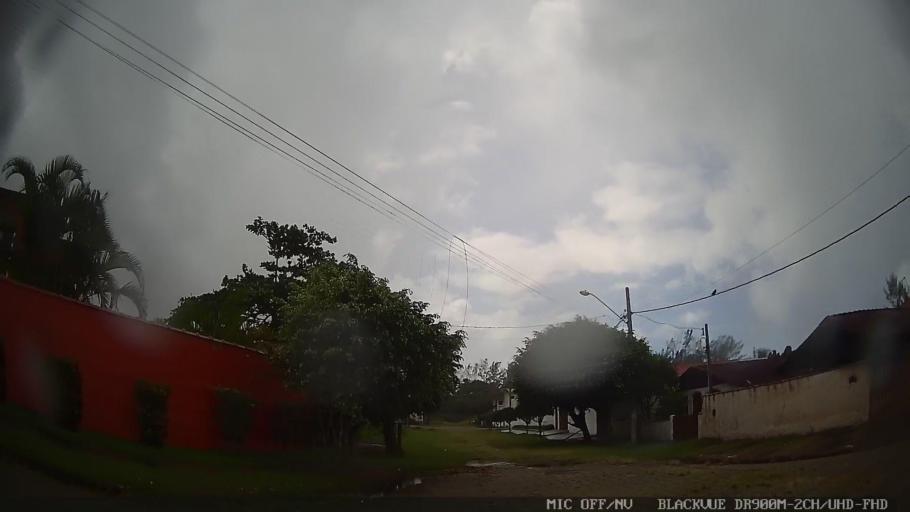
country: BR
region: Sao Paulo
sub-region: Itanhaem
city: Itanhaem
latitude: -24.2221
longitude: -46.8559
